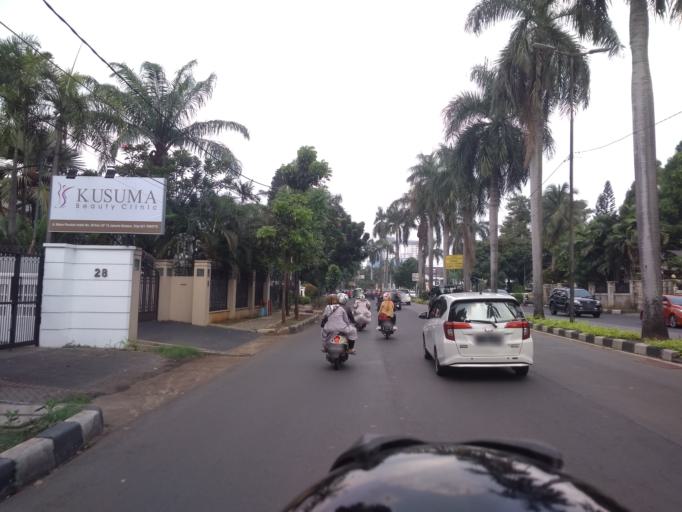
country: ID
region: Banten
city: South Tangerang
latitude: -6.2812
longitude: 106.7805
